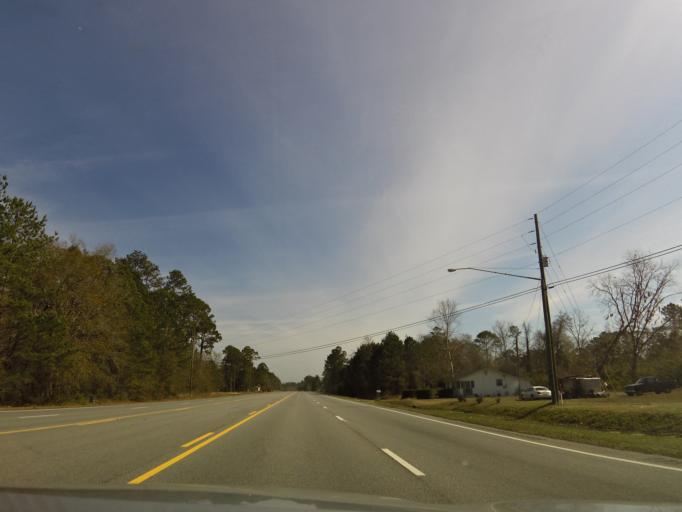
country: US
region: Georgia
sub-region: Lanier County
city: Lakeland
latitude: 30.9099
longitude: -83.0760
